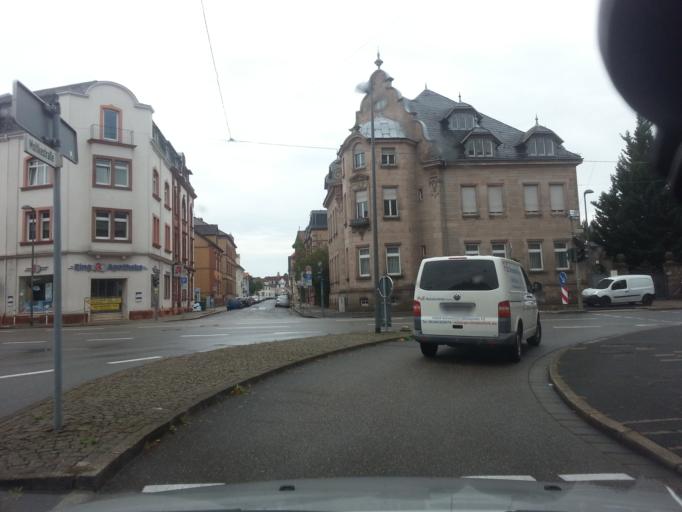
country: DE
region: Rheinland-Pfalz
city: Landau in der Pfalz
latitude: 49.1948
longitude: 8.1185
